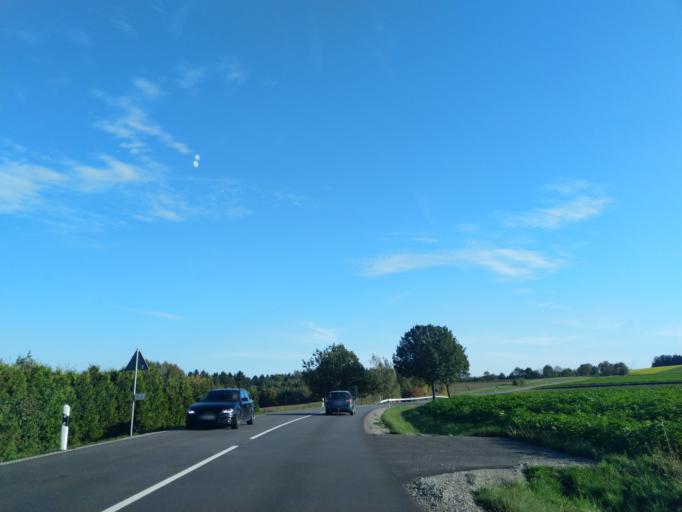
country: DE
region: Bavaria
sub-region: Lower Bavaria
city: Metten
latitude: 48.8664
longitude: 12.9356
